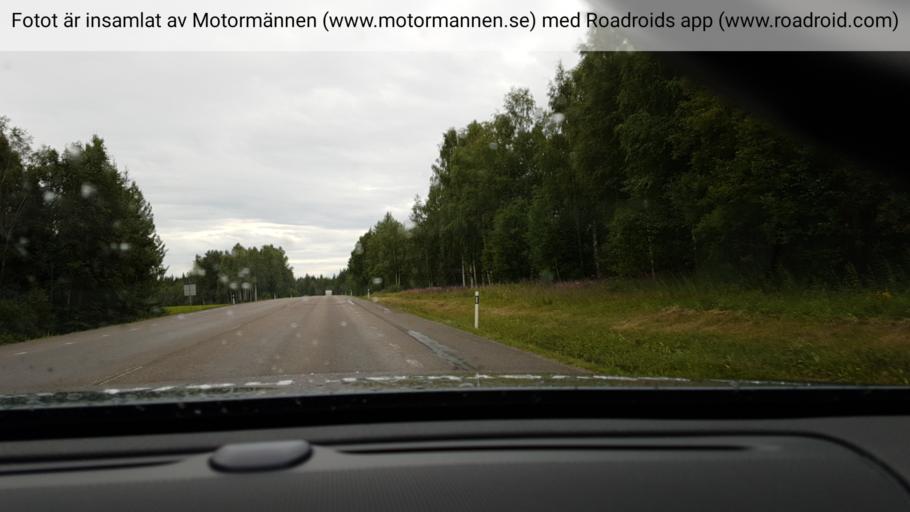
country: SE
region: Dalarna
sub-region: Leksand Municipality
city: Leksand
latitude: 60.7779
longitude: 15.0220
